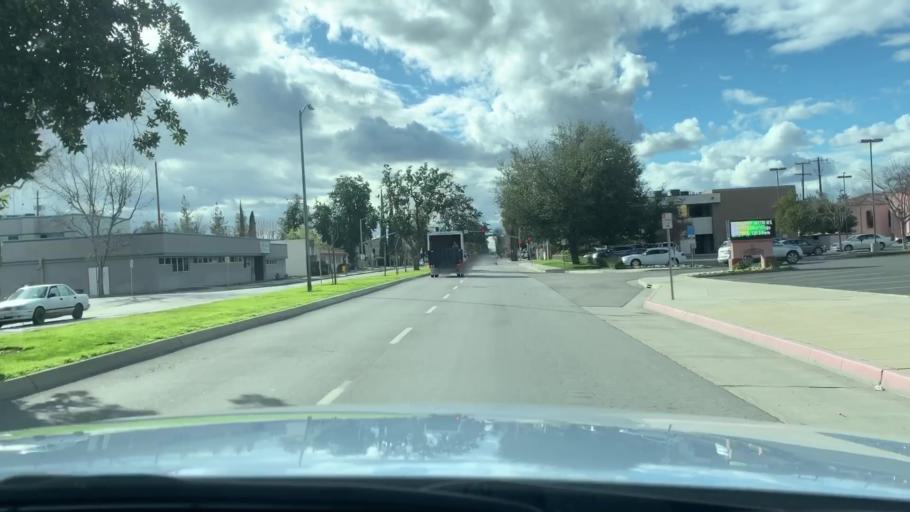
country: US
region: California
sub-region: Kern County
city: Bakersfield
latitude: 35.3734
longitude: -119.0220
